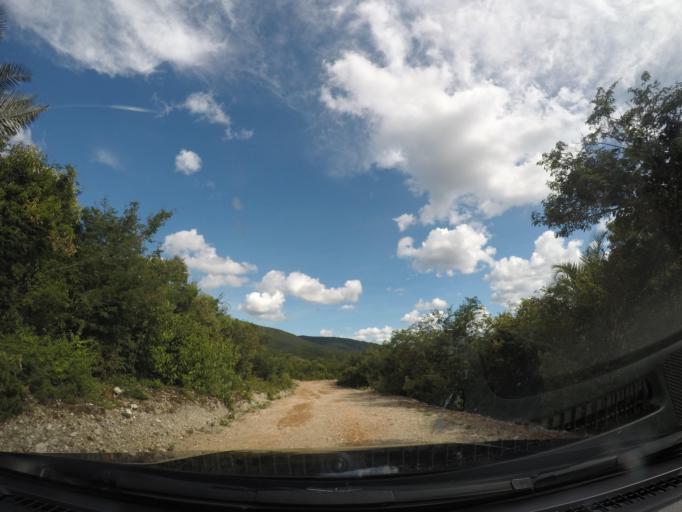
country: BR
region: Bahia
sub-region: Barra Da Estiva
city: Barra da Estiva
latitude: -13.1490
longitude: -41.5967
